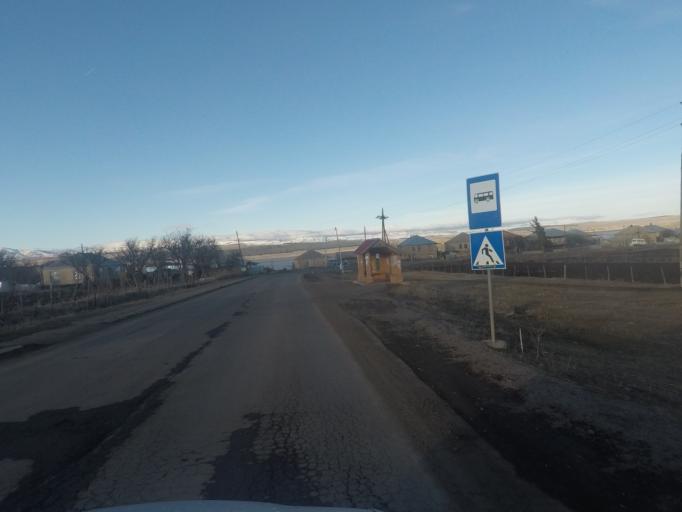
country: GE
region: Kvemo Kartli
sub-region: Tsalka
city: Tsalka
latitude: 41.6024
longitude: 44.0543
